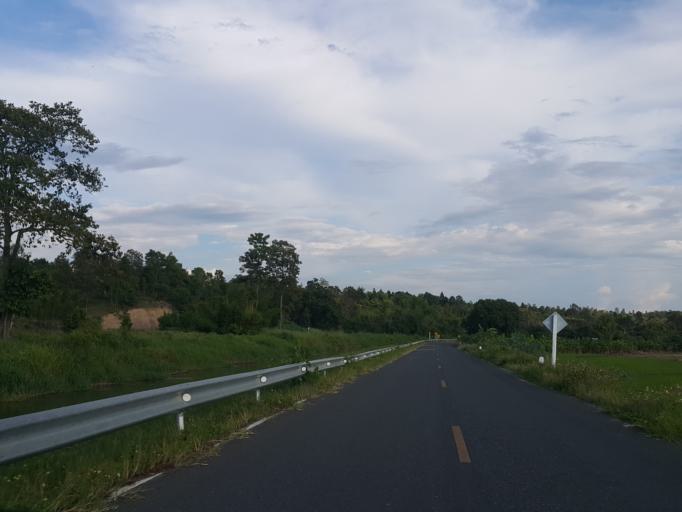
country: TH
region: Chiang Mai
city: San Sai
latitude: 18.9675
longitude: 98.9893
